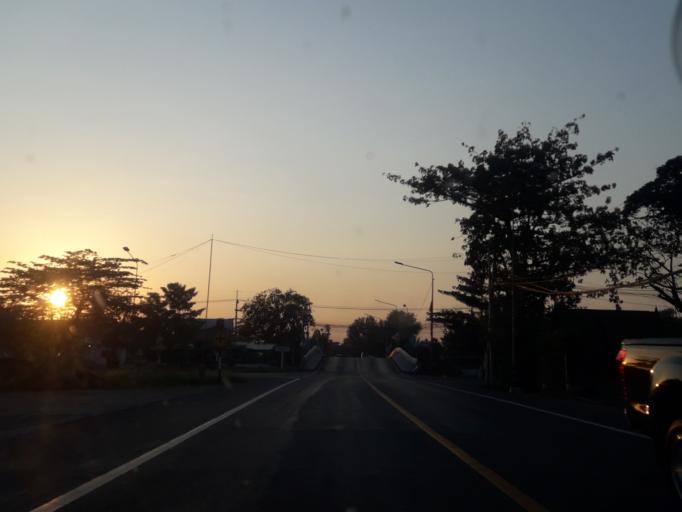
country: TH
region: Pathum Thani
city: Nong Suea
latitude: 14.1319
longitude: 100.7561
